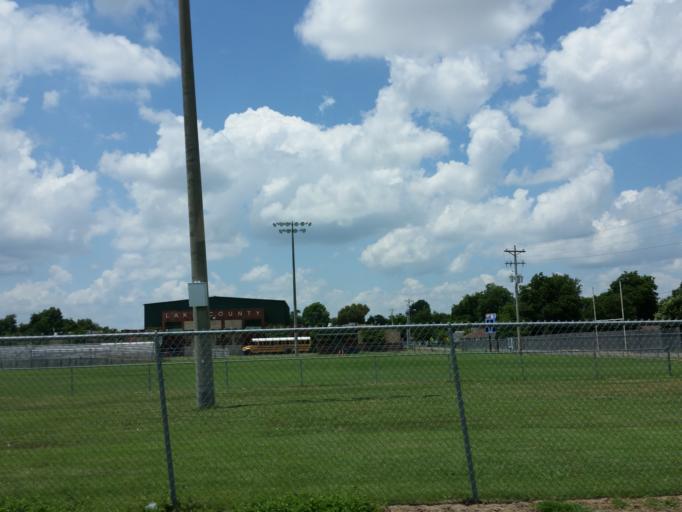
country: US
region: Tennessee
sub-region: Lake County
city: Ridgely
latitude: 36.2659
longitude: -89.4782
